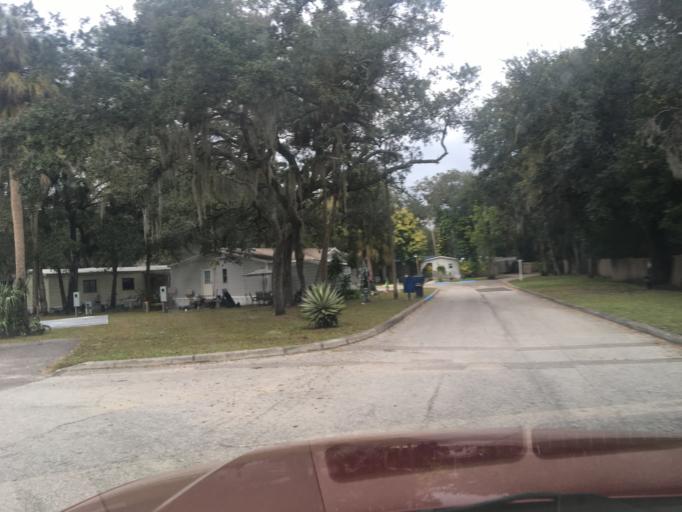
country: US
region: Florida
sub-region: Hillsborough County
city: Gibsonton
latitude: 27.8531
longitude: -82.3580
